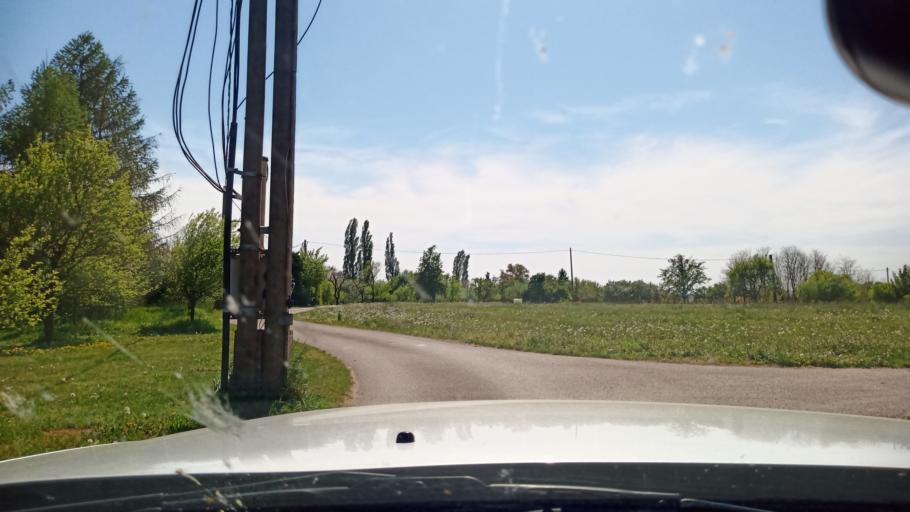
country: HU
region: Zala
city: Heviz
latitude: 46.7598
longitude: 17.1418
